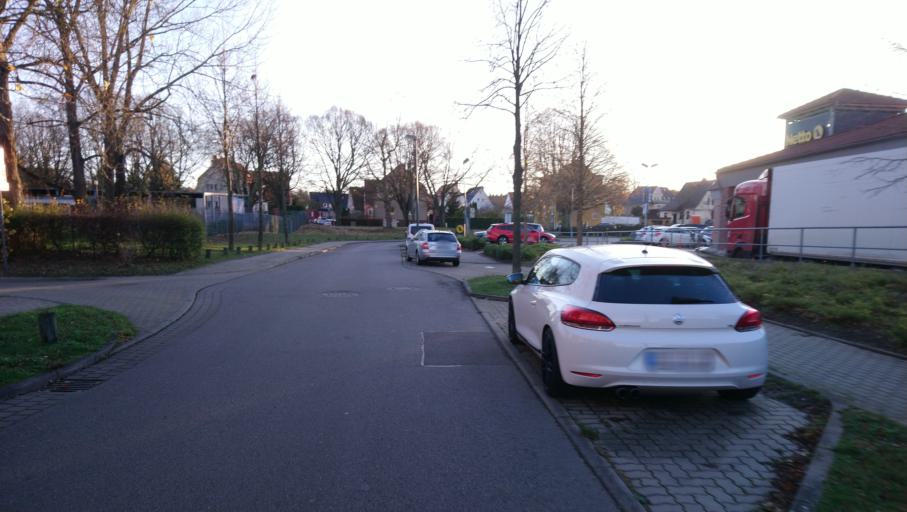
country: DE
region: Mecklenburg-Vorpommern
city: Kritzmow
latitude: 54.0878
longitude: 12.0829
